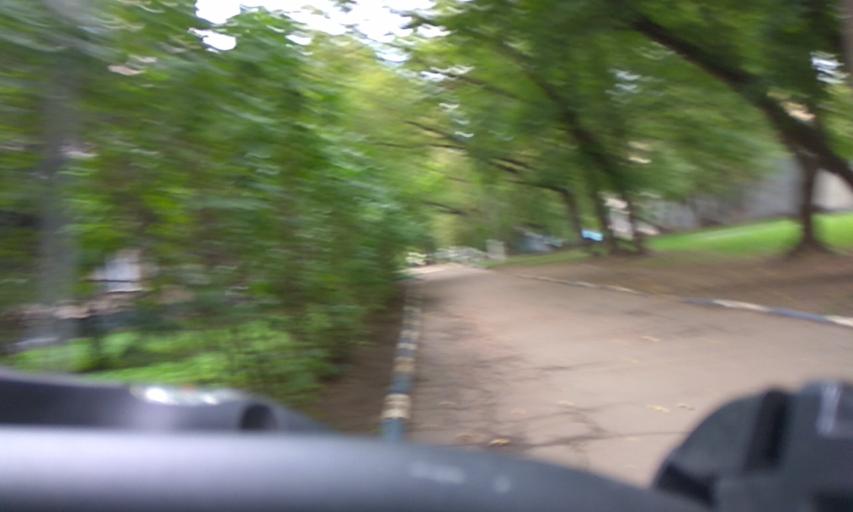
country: RU
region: Moscow
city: Kolomenskoye
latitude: 55.6844
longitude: 37.6921
